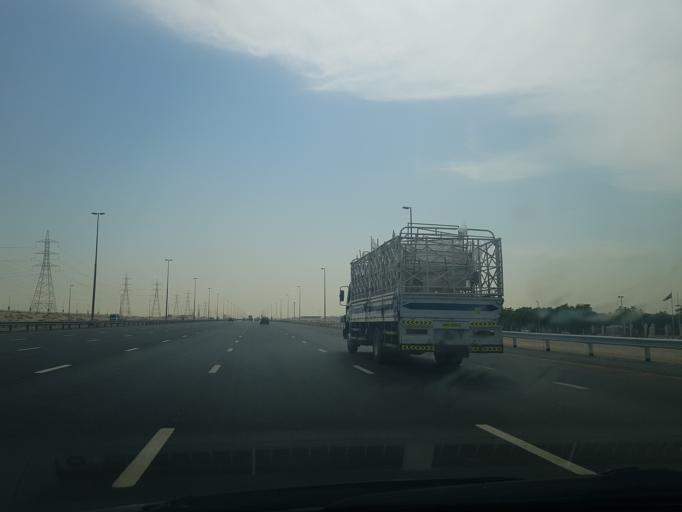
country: AE
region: Ash Shariqah
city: Sharjah
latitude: 25.2665
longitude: 55.5789
